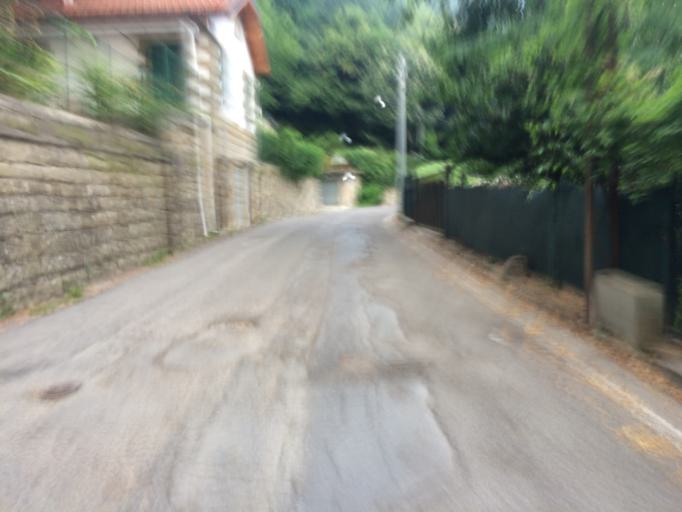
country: IT
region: Liguria
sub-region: Provincia di Imperia
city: Seborga
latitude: 43.8555
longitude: 7.7250
